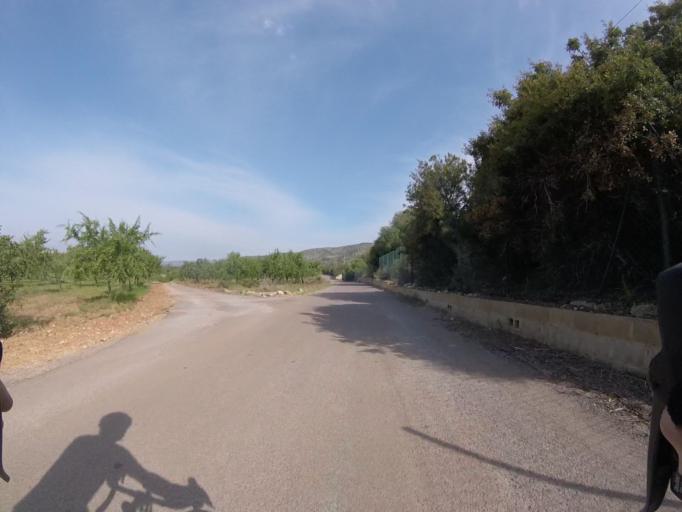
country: ES
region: Valencia
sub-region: Provincia de Castello
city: Alcoceber
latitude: 40.2675
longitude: 0.2528
